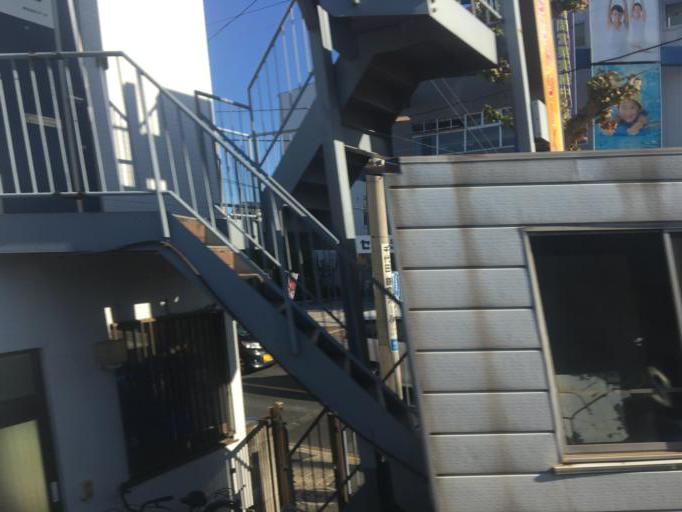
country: JP
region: Chiba
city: Matsudo
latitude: 35.7438
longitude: 139.8814
